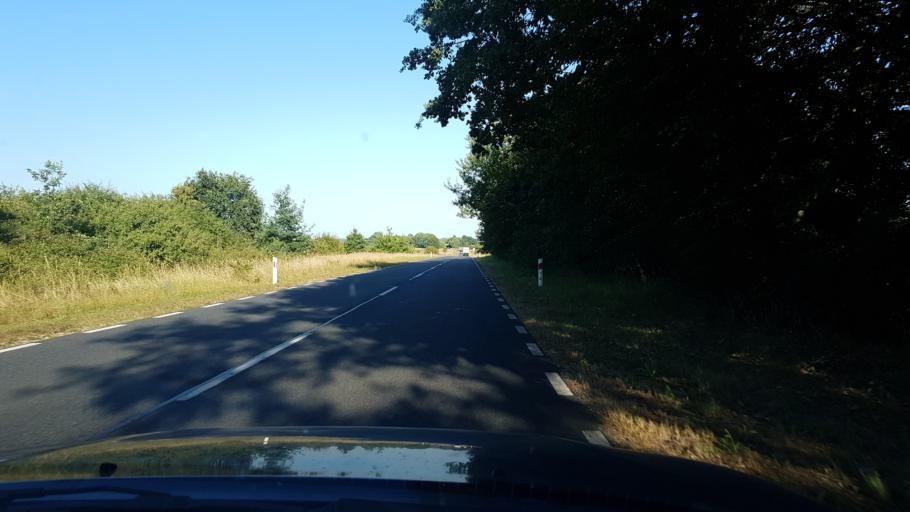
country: PL
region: West Pomeranian Voivodeship
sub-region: Powiat stargardzki
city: Stara Dabrowa
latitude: 53.4331
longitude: 15.1451
